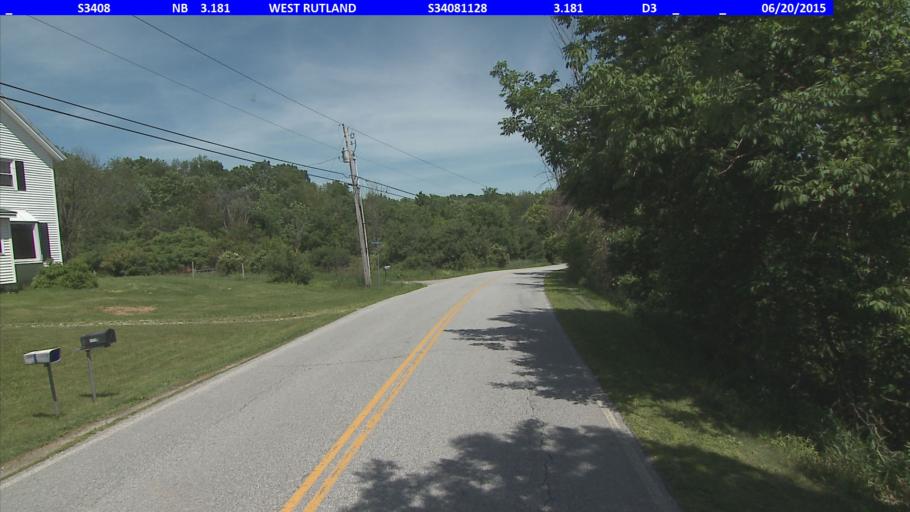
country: US
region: Vermont
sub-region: Rutland County
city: West Rutland
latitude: 43.6546
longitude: -73.0740
